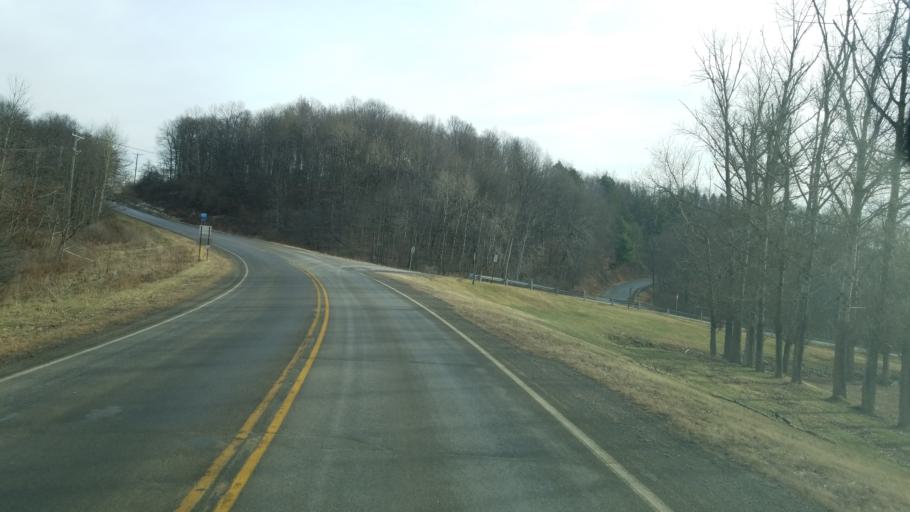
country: US
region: Pennsylvania
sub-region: Jefferson County
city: Punxsutawney
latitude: 40.9522
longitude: -78.9844
